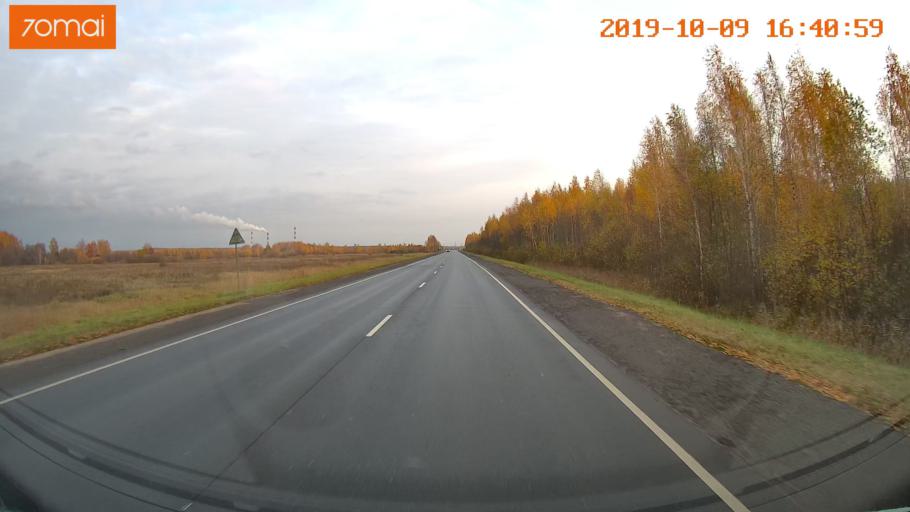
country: RU
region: Kostroma
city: Volgorechensk
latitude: 57.4773
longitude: 41.0714
